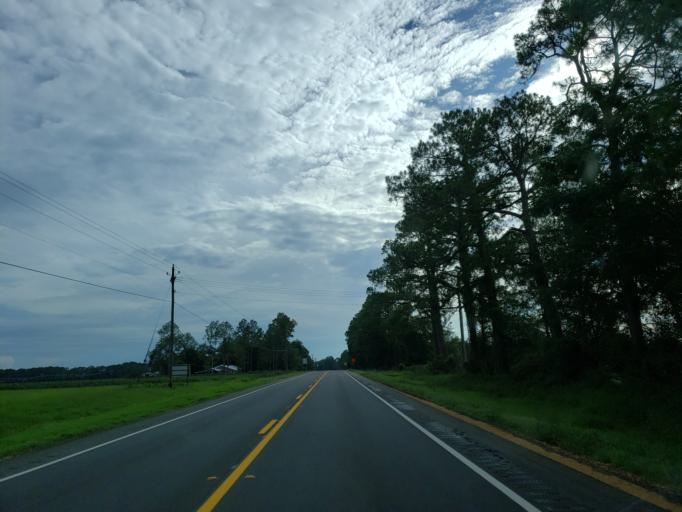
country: US
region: Georgia
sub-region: Irwin County
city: Ocilla
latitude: 31.5830
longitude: -83.2819
